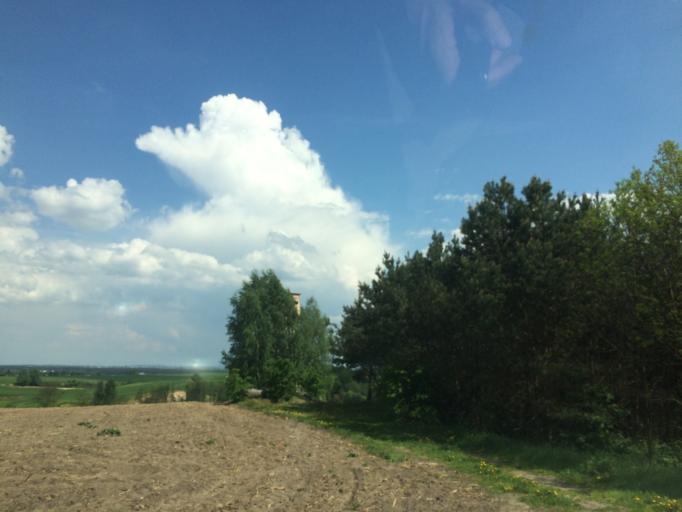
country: PL
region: Warmian-Masurian Voivodeship
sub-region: Powiat nowomiejski
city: Nowe Miasto Lubawskie
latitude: 53.4474
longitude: 19.5808
